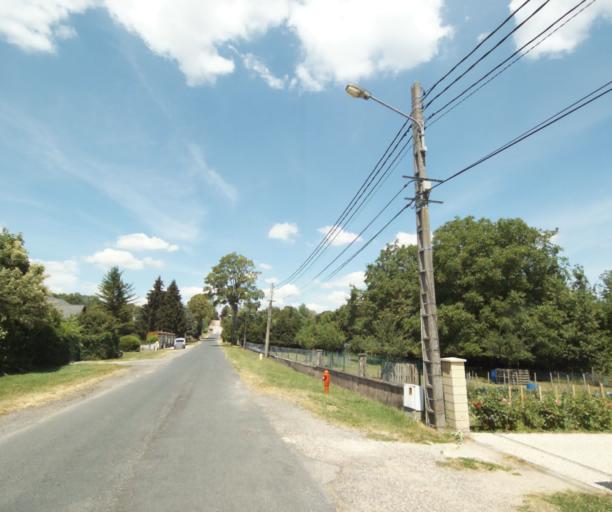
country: FR
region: Lorraine
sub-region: Departement de Meurthe-et-Moselle
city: Luneville
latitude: 48.6065
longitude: 6.4899
